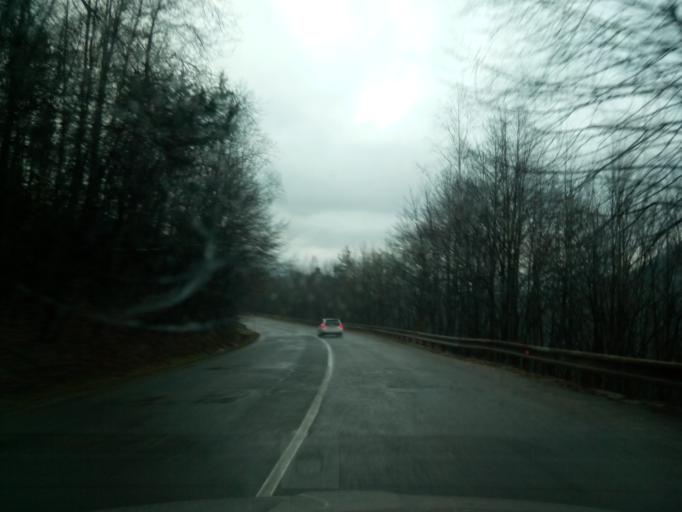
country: SK
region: Kosicky
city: Gelnica
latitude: 48.9052
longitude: 20.9822
